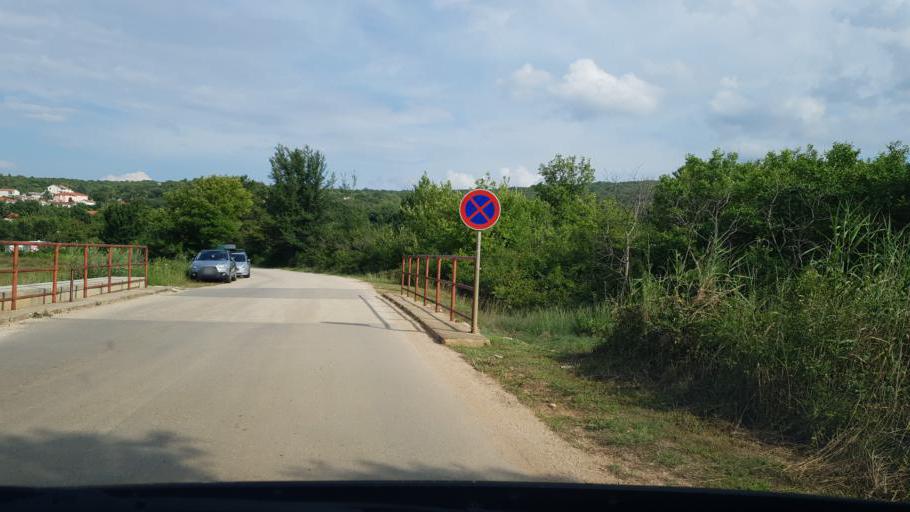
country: HR
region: Primorsko-Goranska
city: Njivice
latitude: 45.1494
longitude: 14.6008
